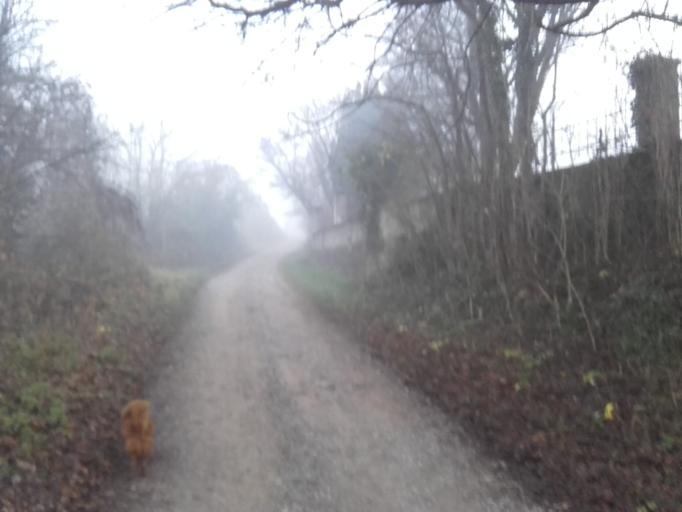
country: SI
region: Sezana
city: Sezana
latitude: 45.7129
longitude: 13.8735
